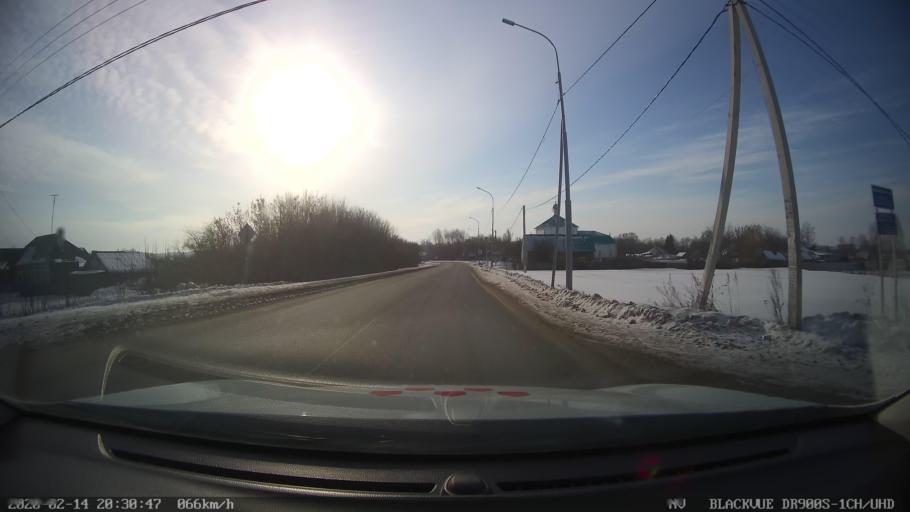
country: RU
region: Tatarstan
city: Stolbishchi
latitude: 55.4403
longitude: 48.9919
